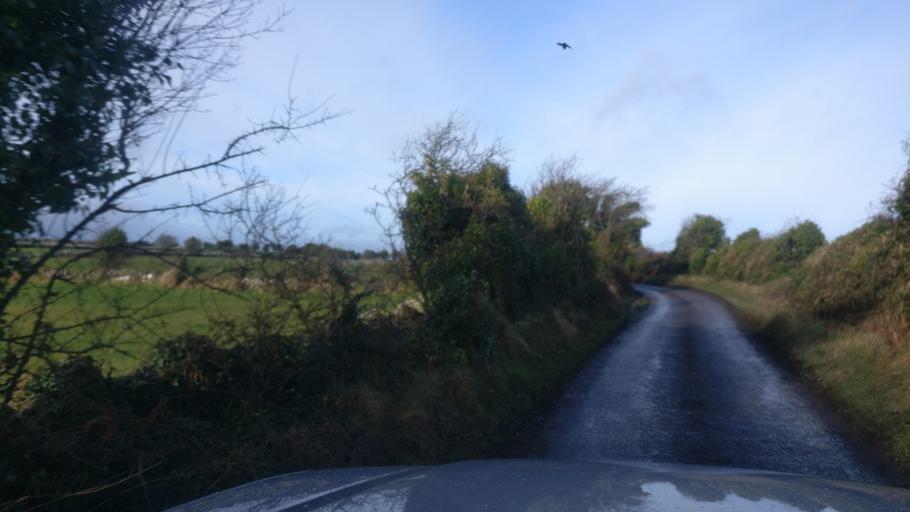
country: IE
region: Connaught
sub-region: County Galway
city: Loughrea
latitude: 53.2013
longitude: -8.6685
